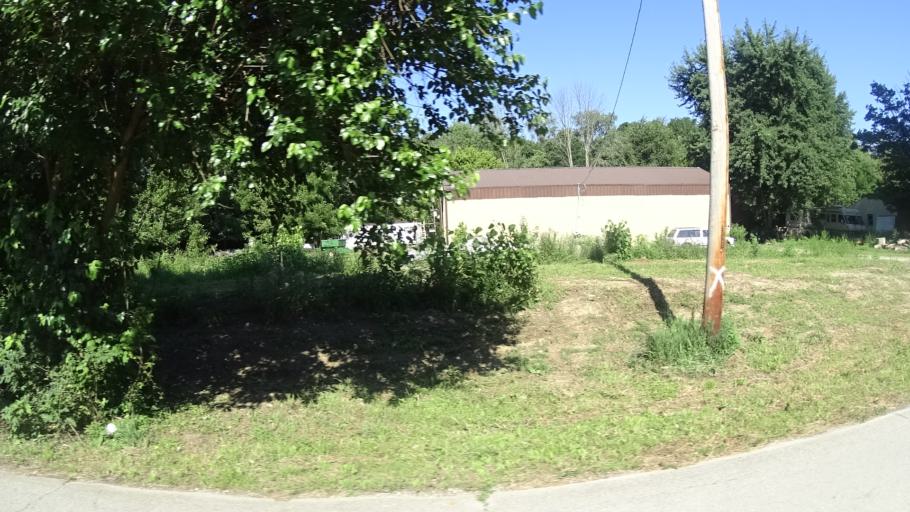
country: US
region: Indiana
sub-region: Madison County
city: Ingalls
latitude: 39.9733
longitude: -85.7962
